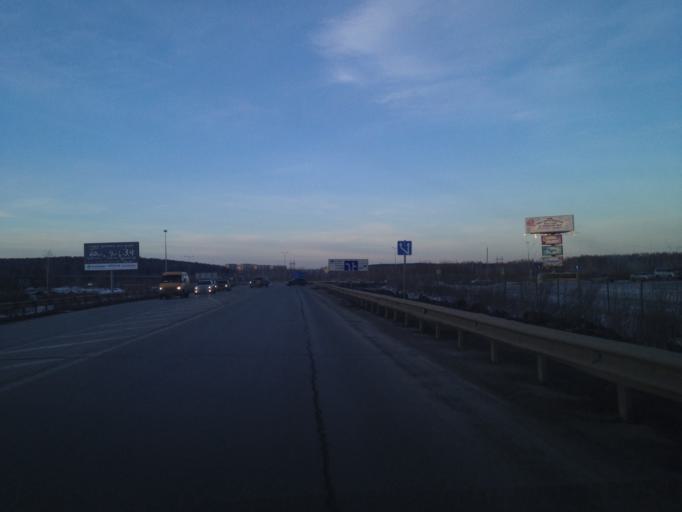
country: RU
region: Sverdlovsk
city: Istok
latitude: 56.7638
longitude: 60.7412
